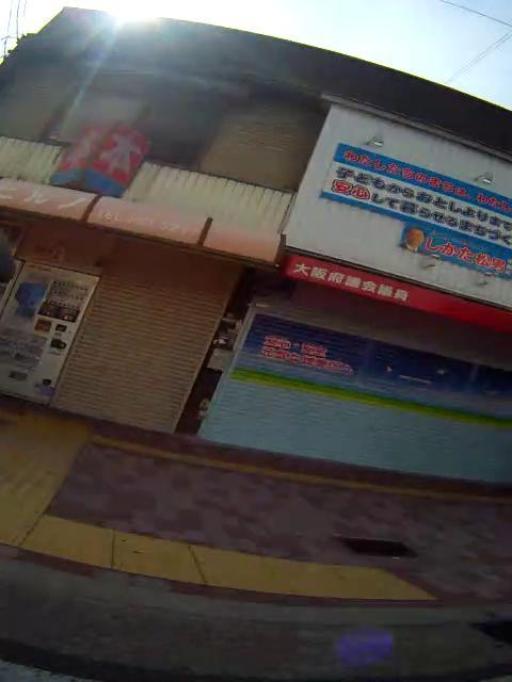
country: JP
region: Osaka
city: Osaka-shi
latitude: 34.6914
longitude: 135.5459
